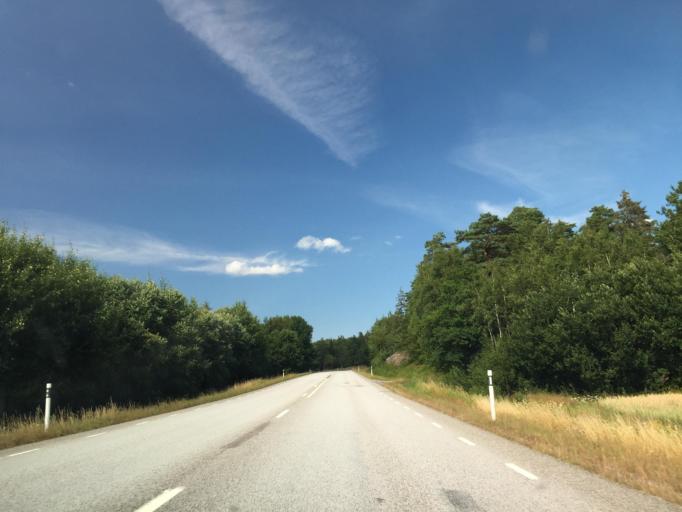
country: SE
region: Vaestra Goetaland
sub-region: Tanums Kommun
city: Tanumshede
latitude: 58.8152
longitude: 11.2628
